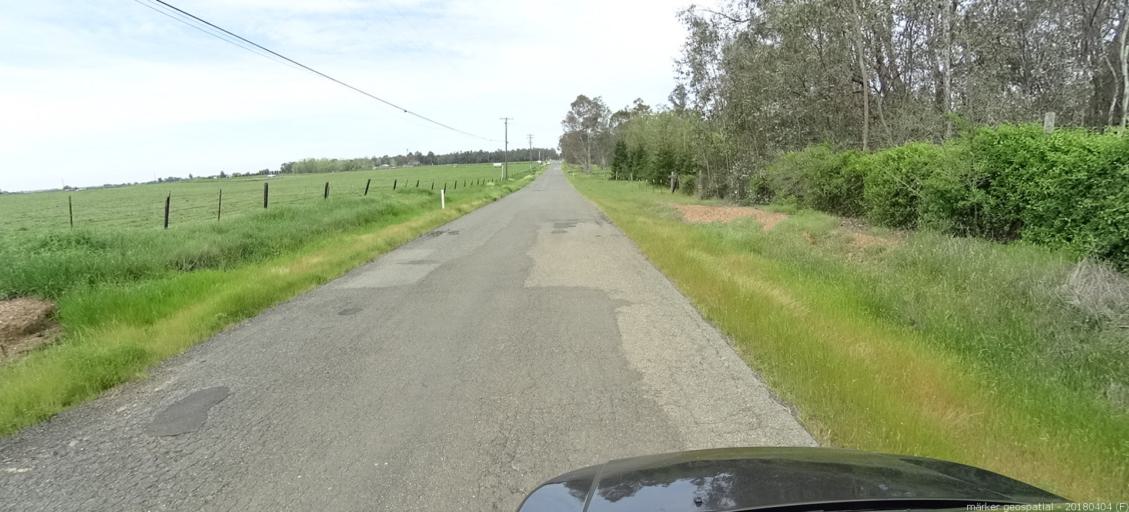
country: US
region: California
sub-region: Sacramento County
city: Clay
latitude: 38.2927
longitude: -121.1670
